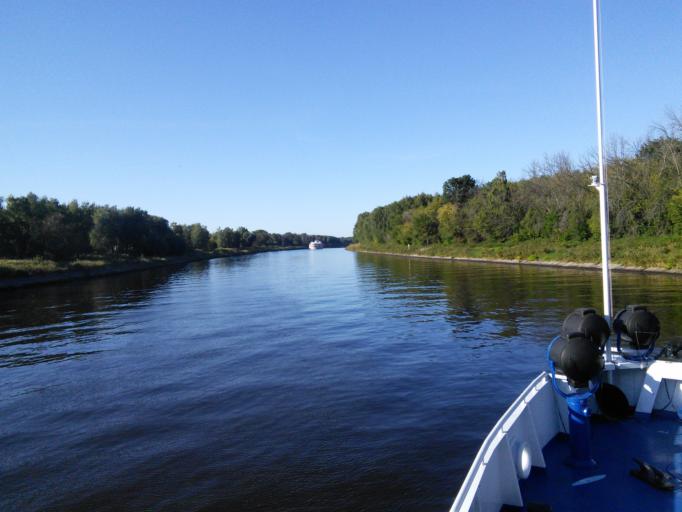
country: RU
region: Moskovskaya
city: Yakhroma
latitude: 56.2987
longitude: 37.4898
